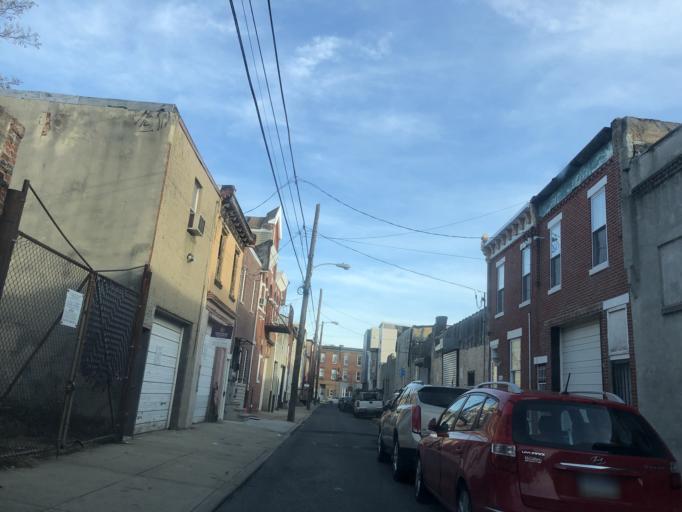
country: US
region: Pennsylvania
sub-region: Philadelphia County
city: Philadelphia
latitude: 39.9265
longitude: -75.1538
